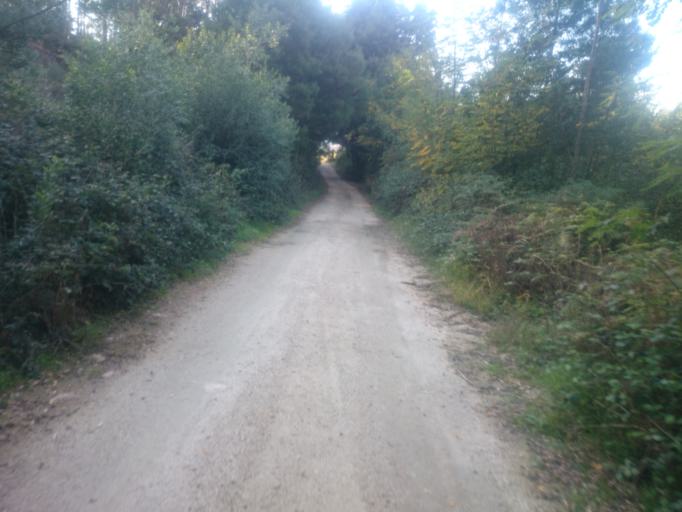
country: ES
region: Galicia
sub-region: Provincia de Pontevedra
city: Porrino
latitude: 42.1566
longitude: -8.6065
